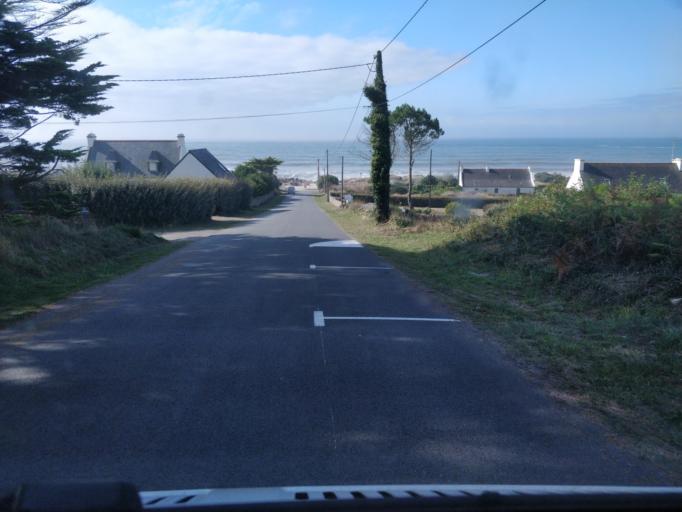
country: FR
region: Brittany
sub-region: Departement du Finistere
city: Plouhinec
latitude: 48.0031
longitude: -4.4976
